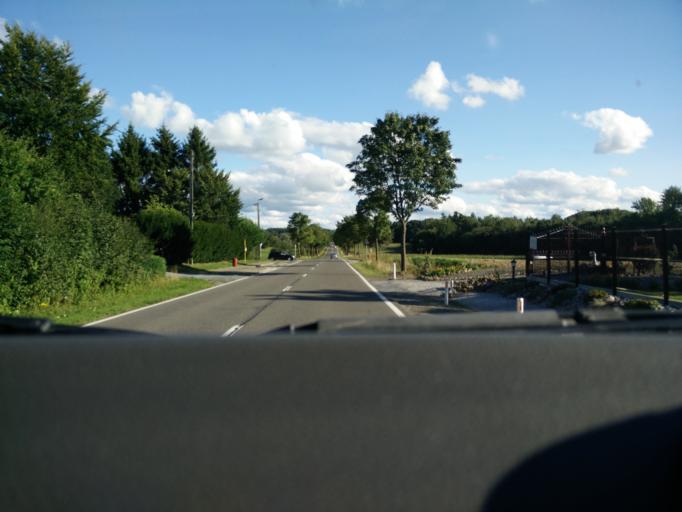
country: BE
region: Wallonia
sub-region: Province du Hainaut
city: Beaumont
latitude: 50.2609
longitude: 4.2202
